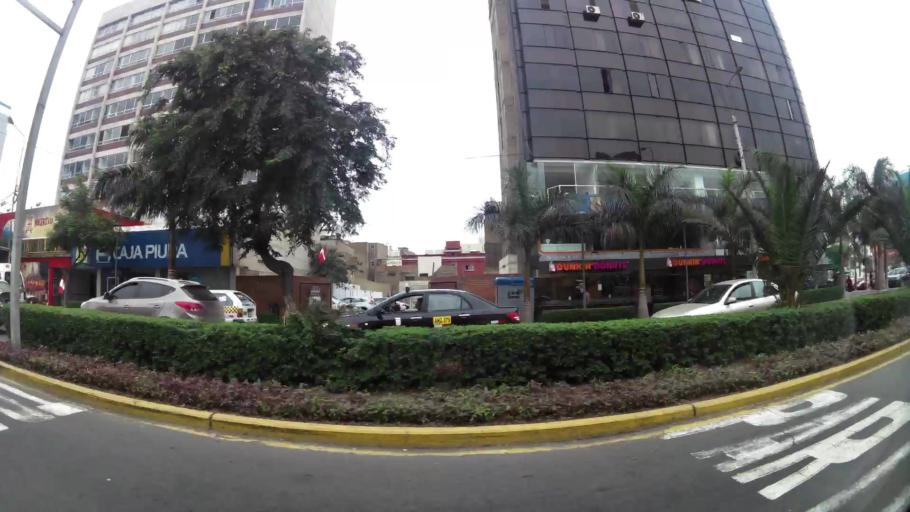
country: PE
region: Lima
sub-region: Lima
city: San Isidro
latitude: -12.1190
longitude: -77.0284
